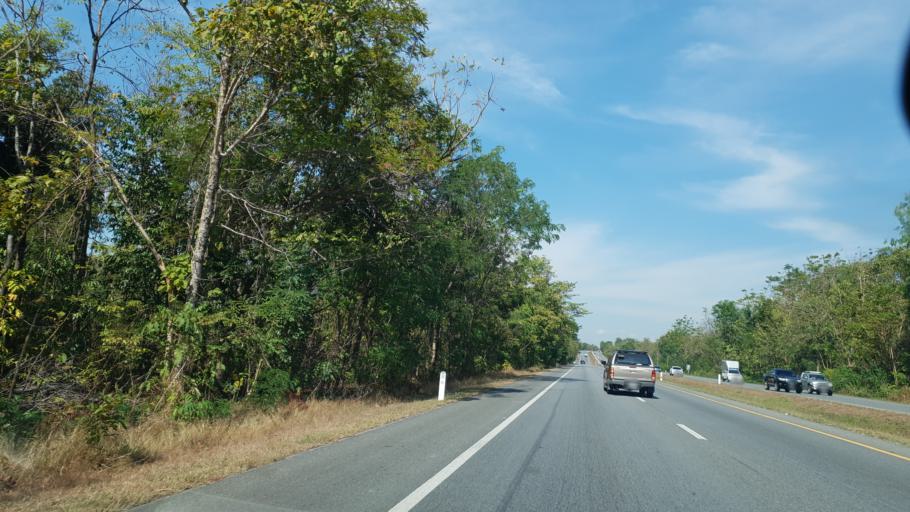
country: TH
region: Uttaradit
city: Thong Saen Khan
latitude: 17.4130
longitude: 100.2283
